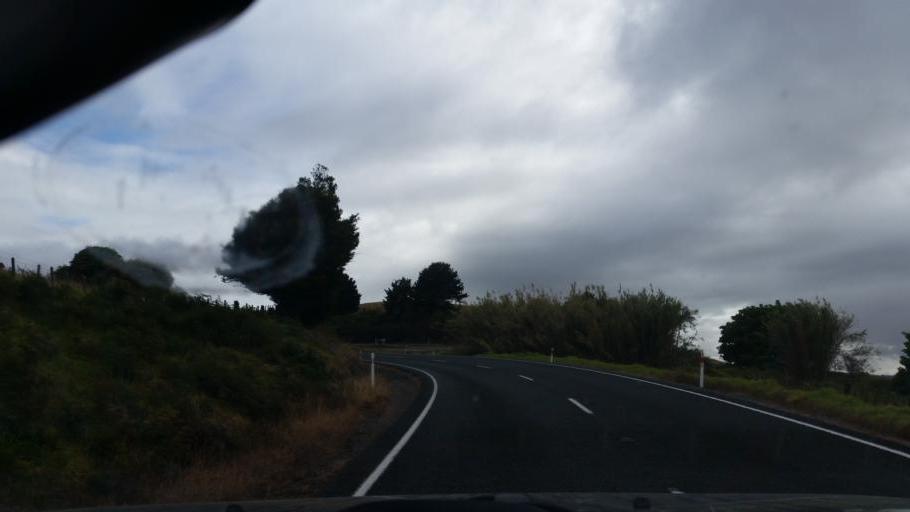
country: NZ
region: Auckland
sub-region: Auckland
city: Wellsford
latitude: -36.1854
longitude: 174.4114
